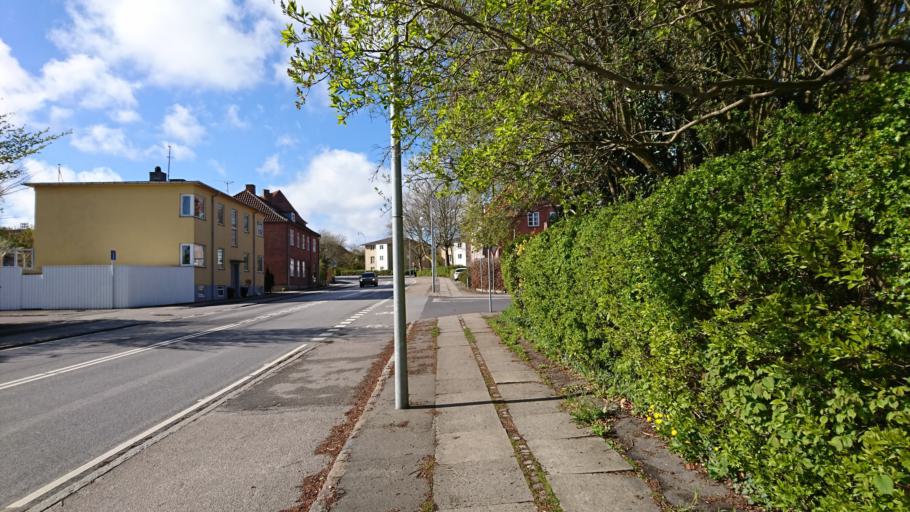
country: DK
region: Zealand
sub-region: Roskilde Kommune
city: Roskilde
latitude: 55.6416
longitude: 12.0723
